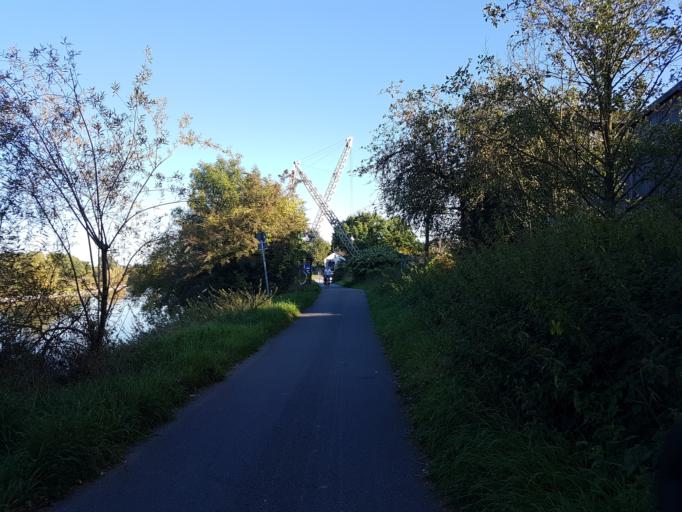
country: DE
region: North Rhine-Westphalia
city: Bad Oeynhausen
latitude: 52.2163
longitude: 8.8339
